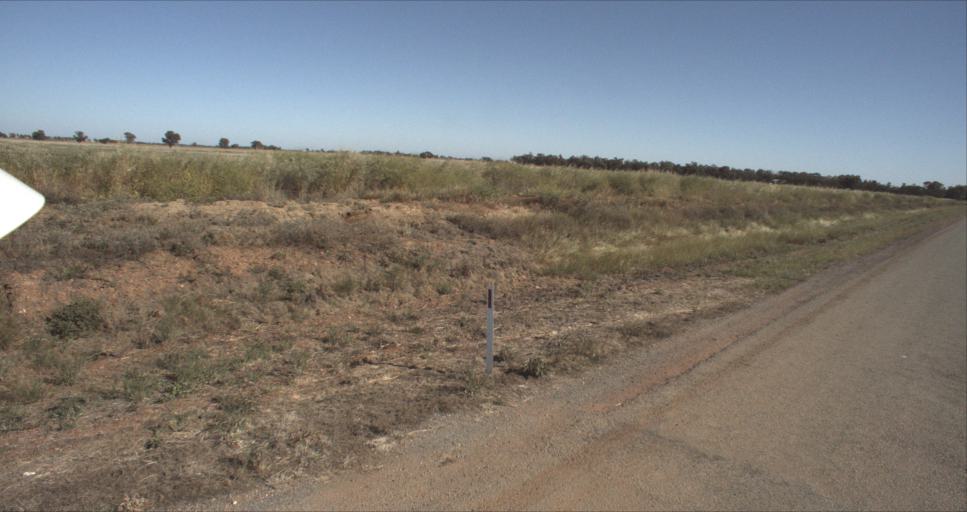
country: AU
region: New South Wales
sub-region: Leeton
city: Leeton
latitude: -34.5832
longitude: 146.3084
